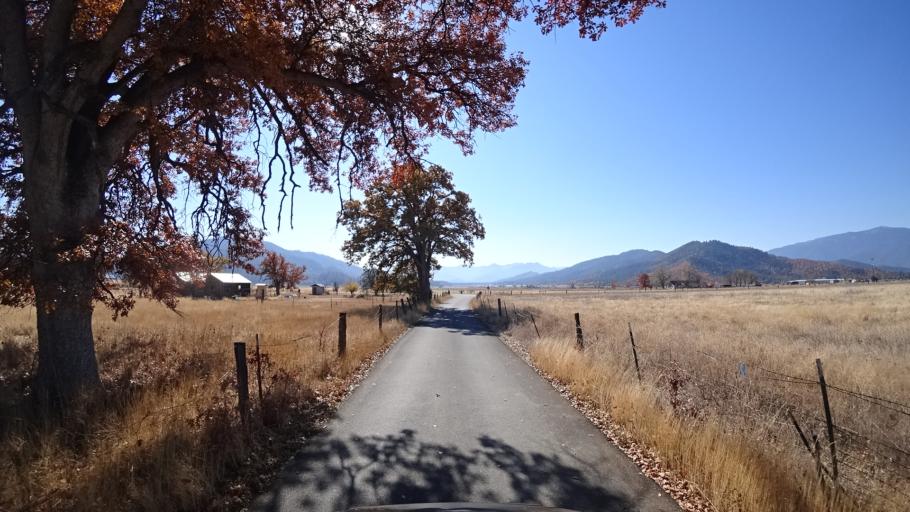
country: US
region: California
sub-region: Siskiyou County
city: Yreka
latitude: 41.6307
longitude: -122.8895
